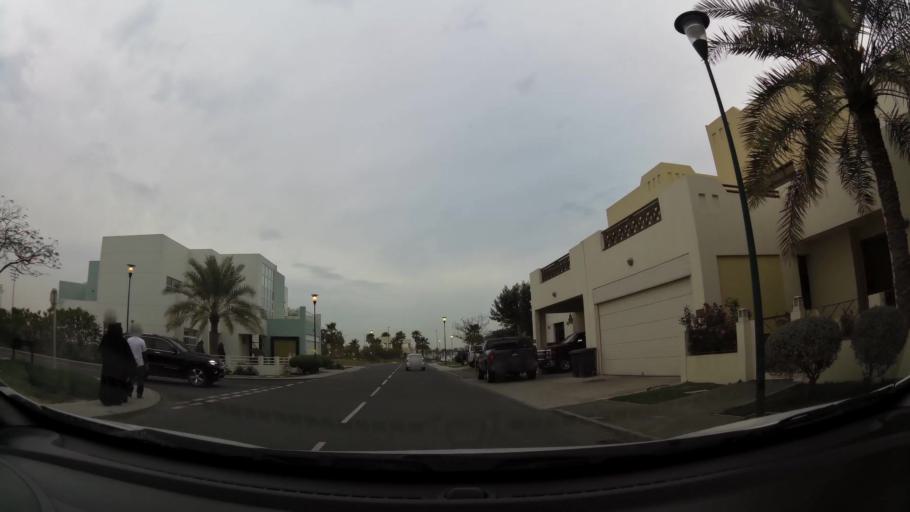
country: BH
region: Northern
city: Ar Rifa'
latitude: 26.1012
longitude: 50.5666
